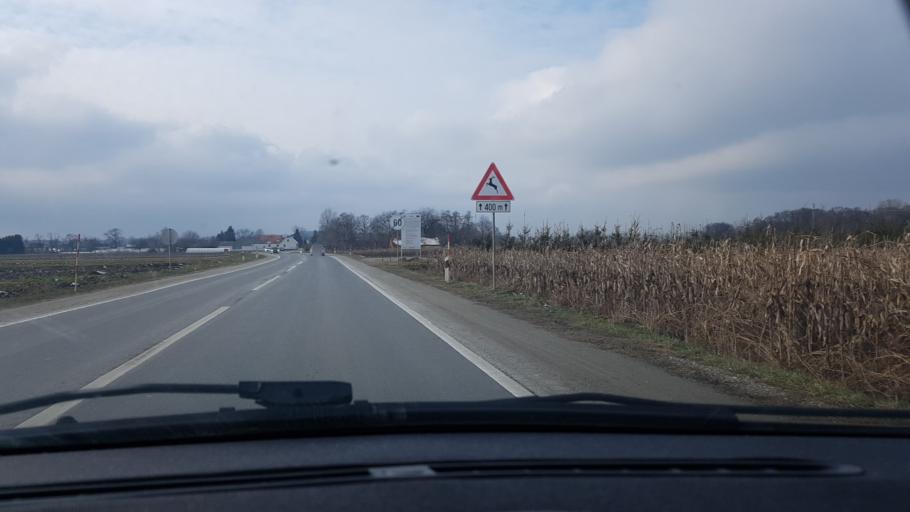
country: HR
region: Varazdinska
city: Tuzno
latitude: 46.2825
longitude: 16.2304
